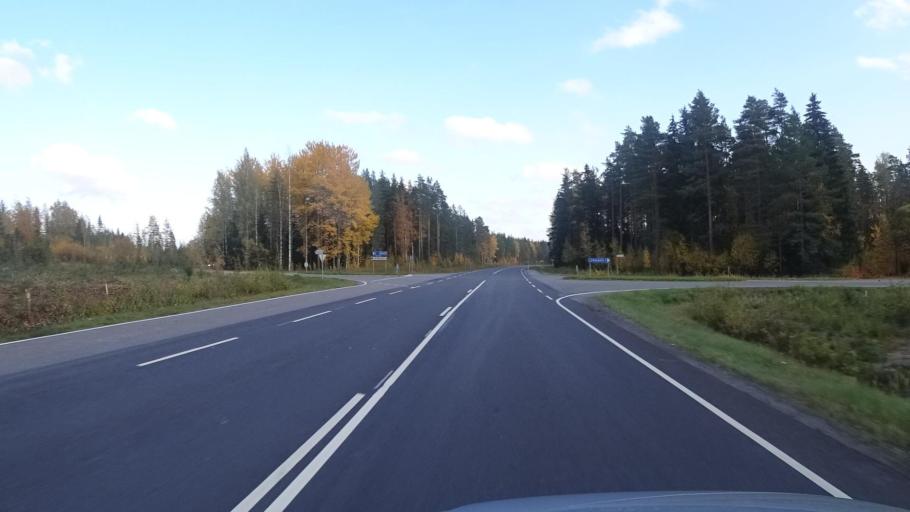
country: FI
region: Satakunta
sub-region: Rauma
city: Koeylioe
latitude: 61.1059
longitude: 22.2239
